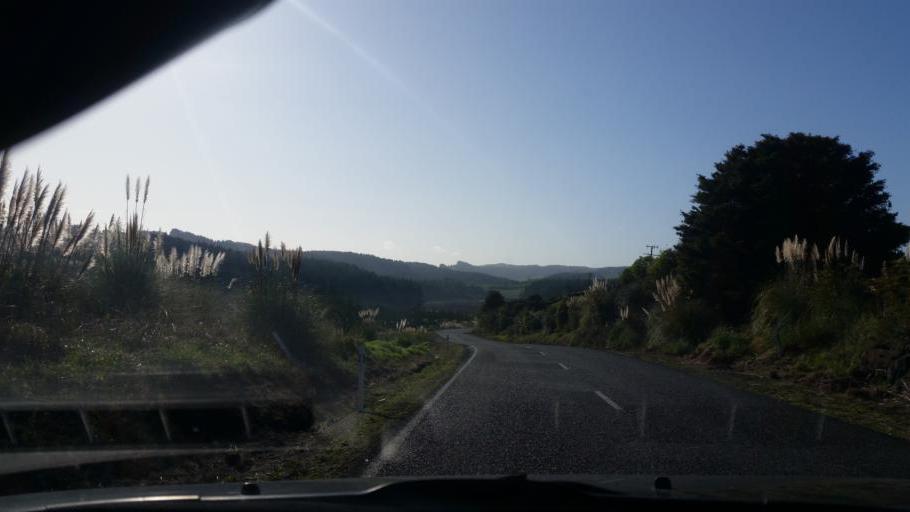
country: NZ
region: Auckland
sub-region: Auckland
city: Wellsford
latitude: -36.2226
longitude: 174.4579
